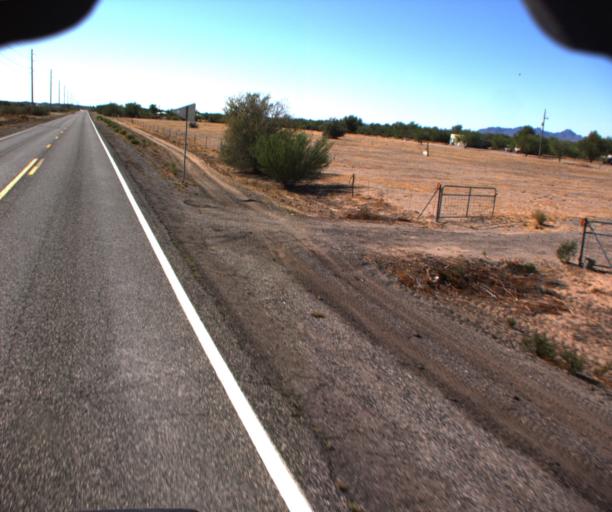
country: US
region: Arizona
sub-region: La Paz County
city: Cienega Springs
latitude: 33.9558
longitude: -114.0265
